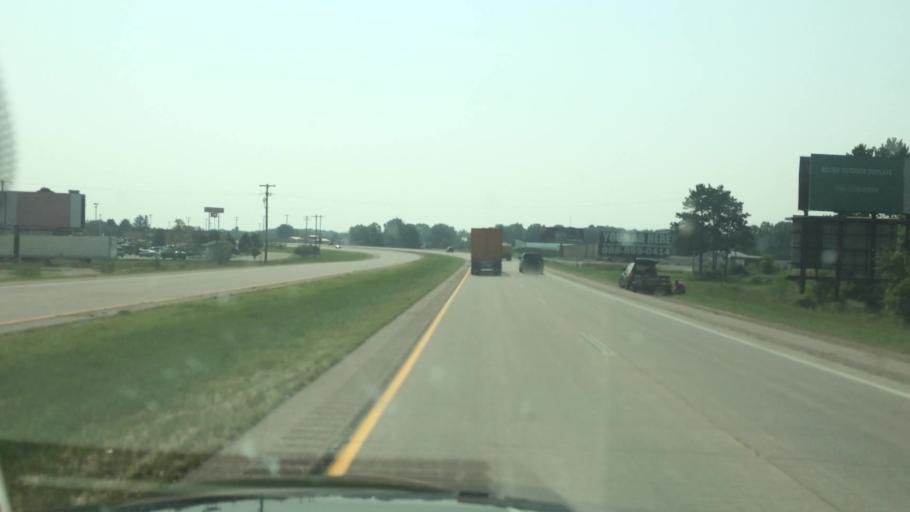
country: US
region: Wisconsin
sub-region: Waupaca County
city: Waupaca
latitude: 44.3322
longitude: -89.0524
